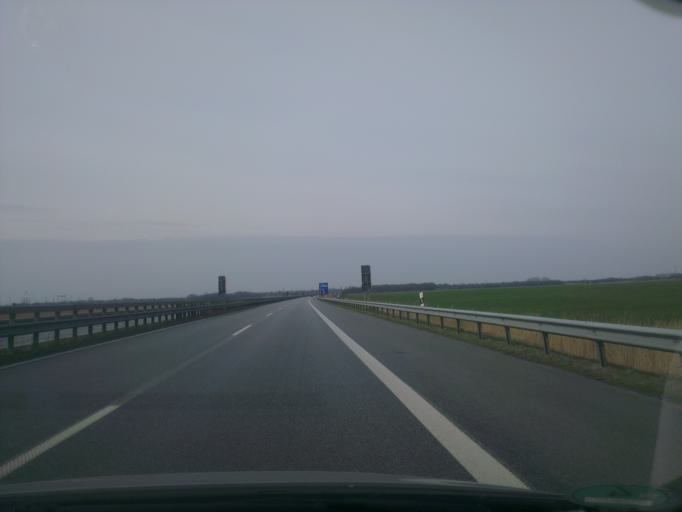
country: DE
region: Lower Saxony
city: Emden
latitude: 53.3647
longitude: 7.2635
